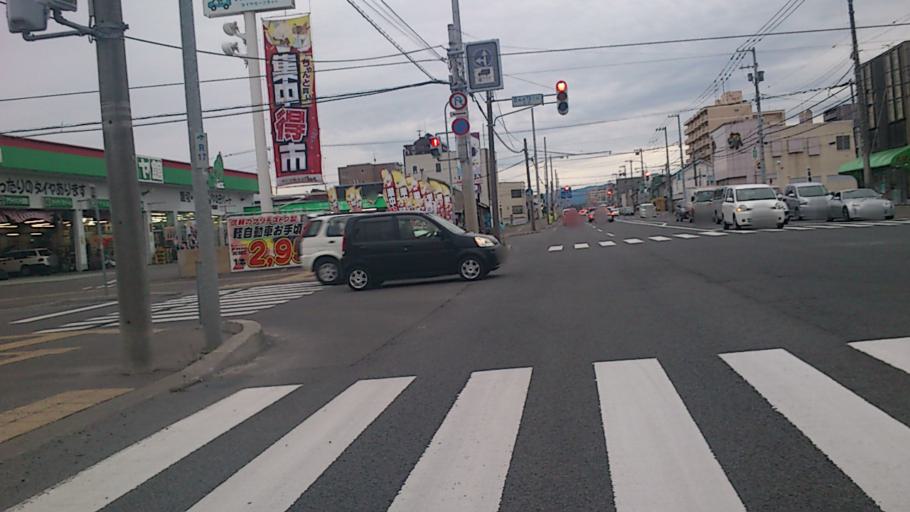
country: JP
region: Hokkaido
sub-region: Asahikawa-shi
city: Asahikawa
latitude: 43.7686
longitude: 142.3803
